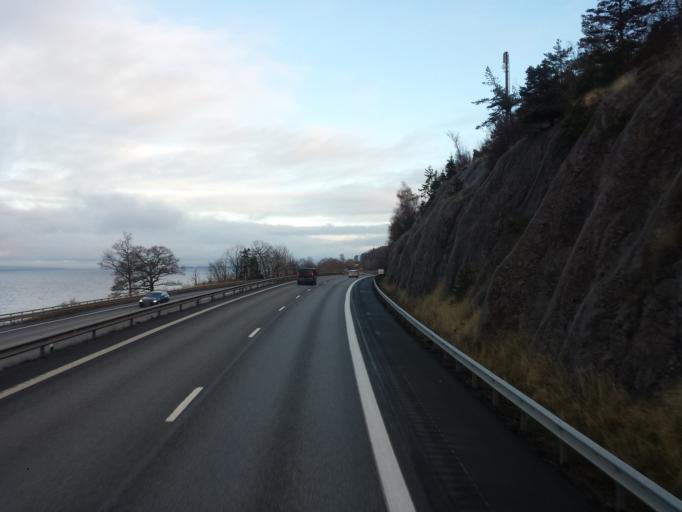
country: SE
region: Joenkoeping
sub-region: Jonkopings Kommun
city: Kaxholmen
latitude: 57.8693
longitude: 14.2717
